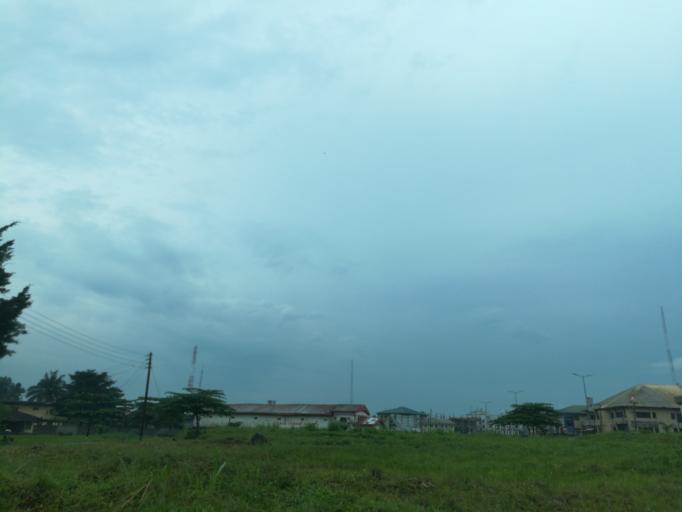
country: NG
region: Rivers
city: Port Harcourt
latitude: 4.8077
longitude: 7.0116
